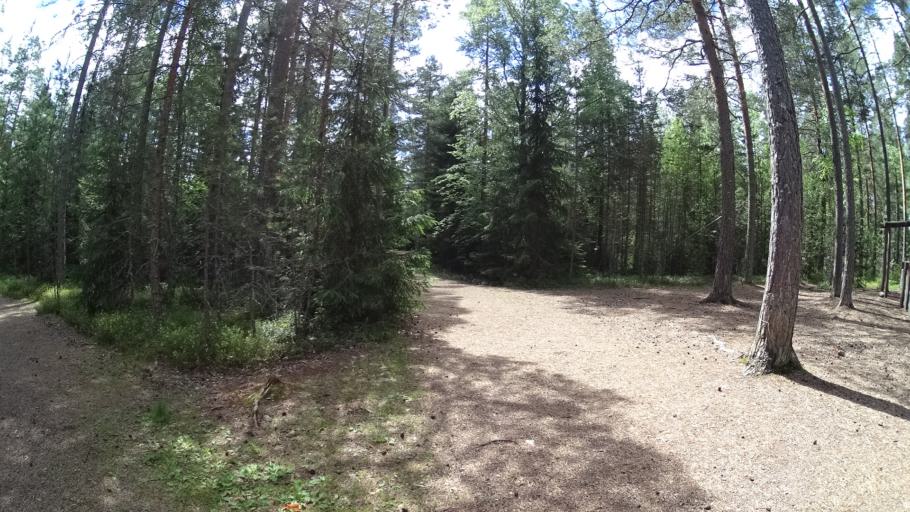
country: FI
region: Uusimaa
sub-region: Helsinki
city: Espoo
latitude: 60.2975
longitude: 24.5587
